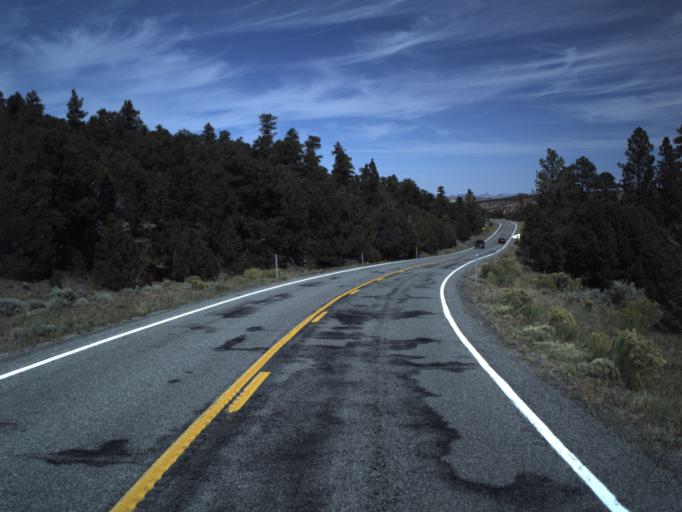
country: US
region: Utah
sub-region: Wayne County
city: Loa
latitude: 38.1890
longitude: -111.3529
